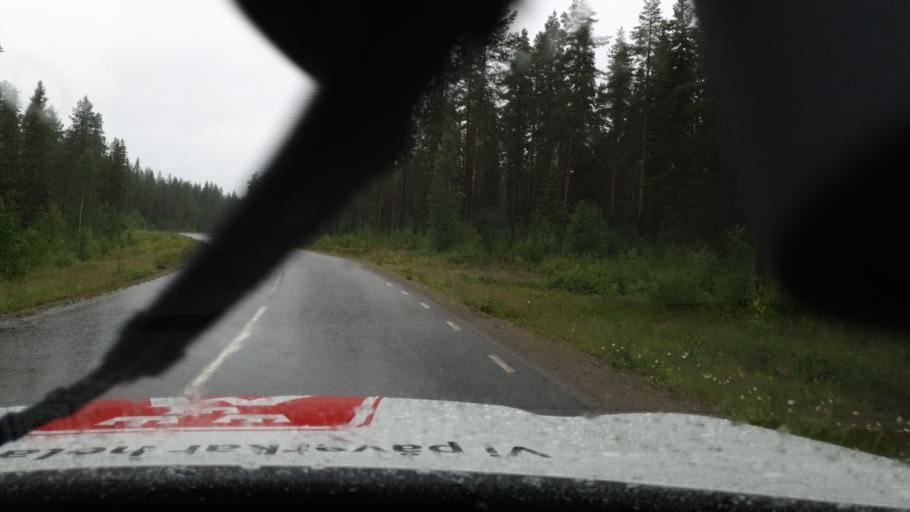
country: SE
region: Vaesterbotten
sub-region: Skelleftea Kommun
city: Langsele
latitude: 64.8375
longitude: 19.8945
